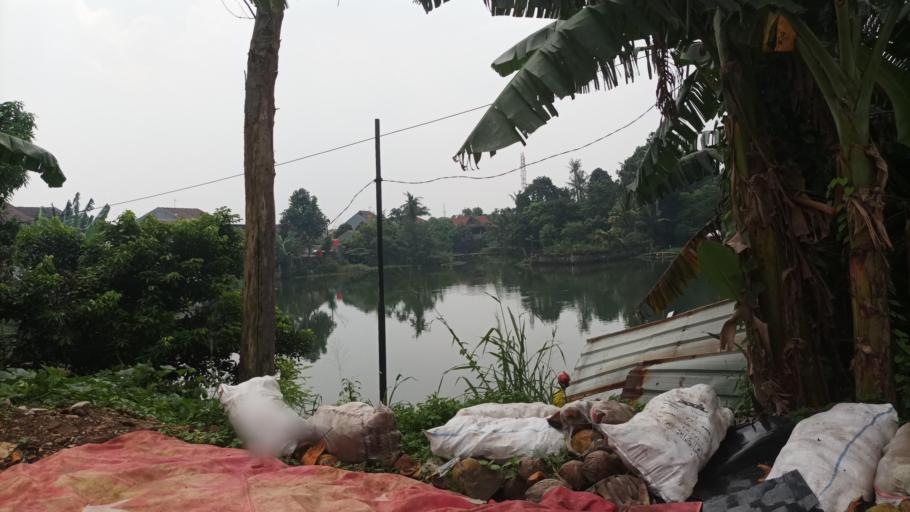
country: ID
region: West Java
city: Depok
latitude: -6.3799
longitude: 106.8596
